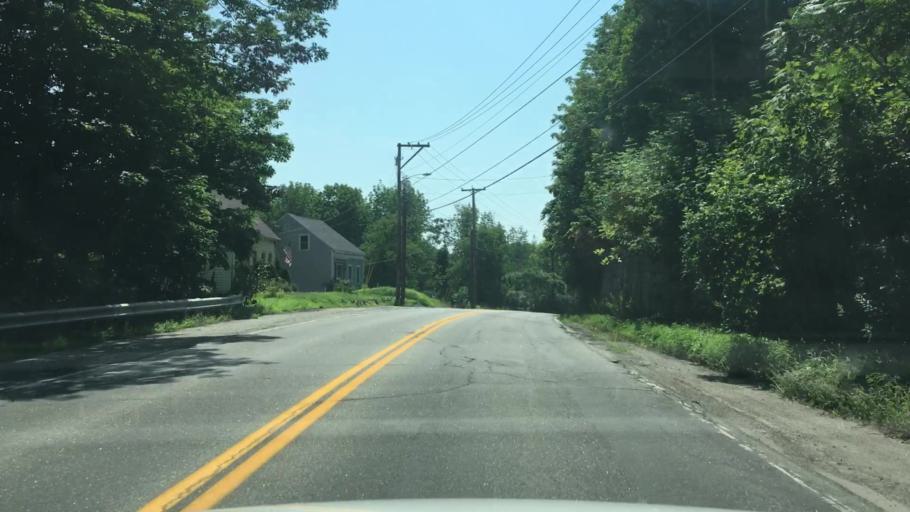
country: US
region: Maine
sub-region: Kennebec County
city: Hallowell
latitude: 44.2712
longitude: -69.7906
